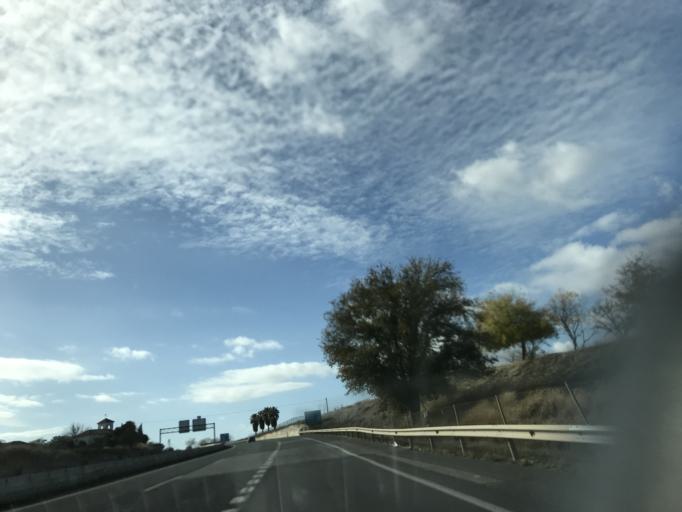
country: ES
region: Andalusia
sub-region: Provincia de Sevilla
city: Ecija
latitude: 37.5309
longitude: -5.0950
